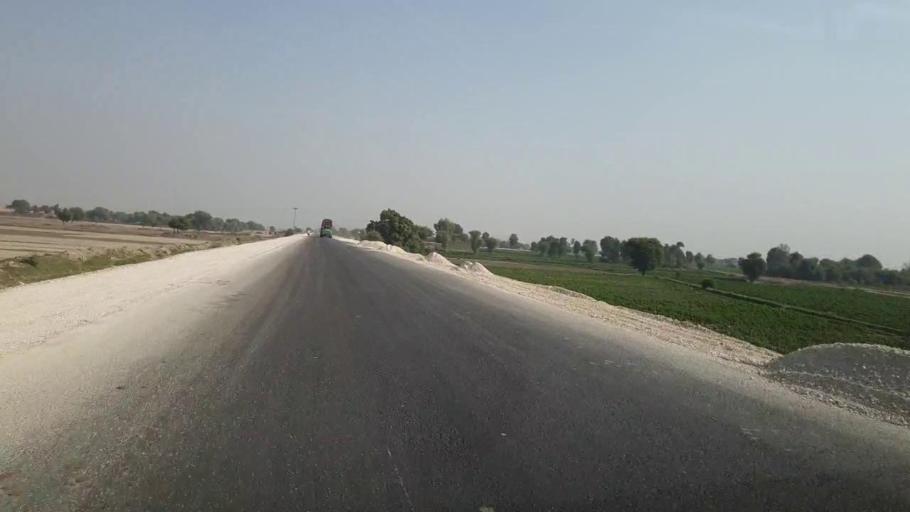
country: PK
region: Sindh
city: Bhan
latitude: 26.5506
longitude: 67.7826
